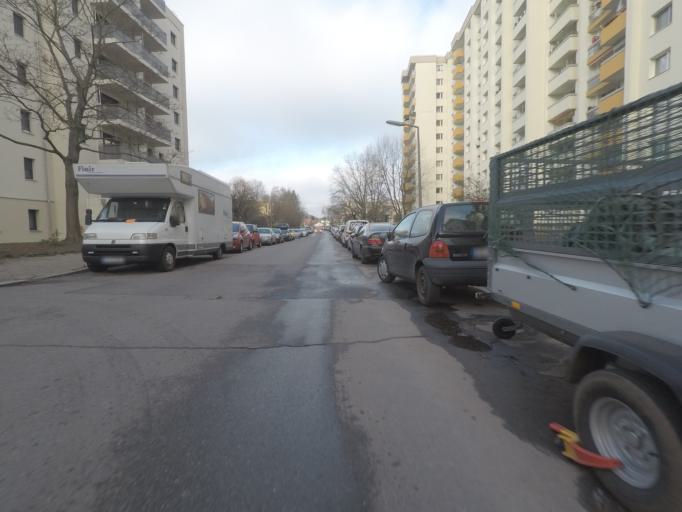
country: DE
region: Berlin
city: Marienfelde
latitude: 52.4100
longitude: 13.3474
